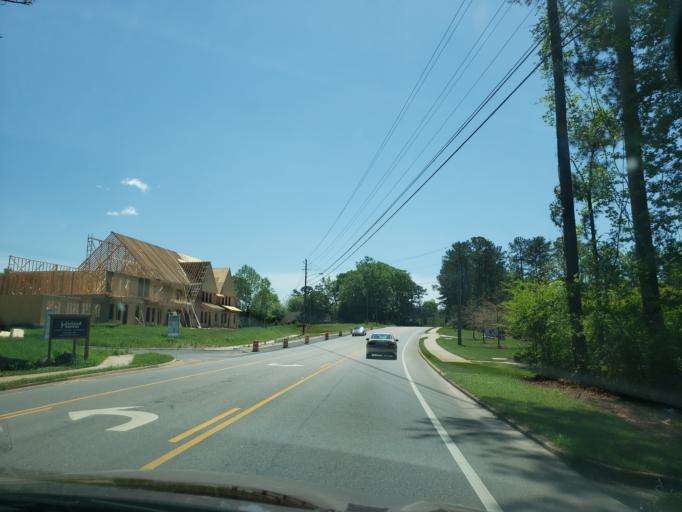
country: US
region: Alabama
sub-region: Lee County
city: Auburn
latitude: 32.6279
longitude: -85.4958
